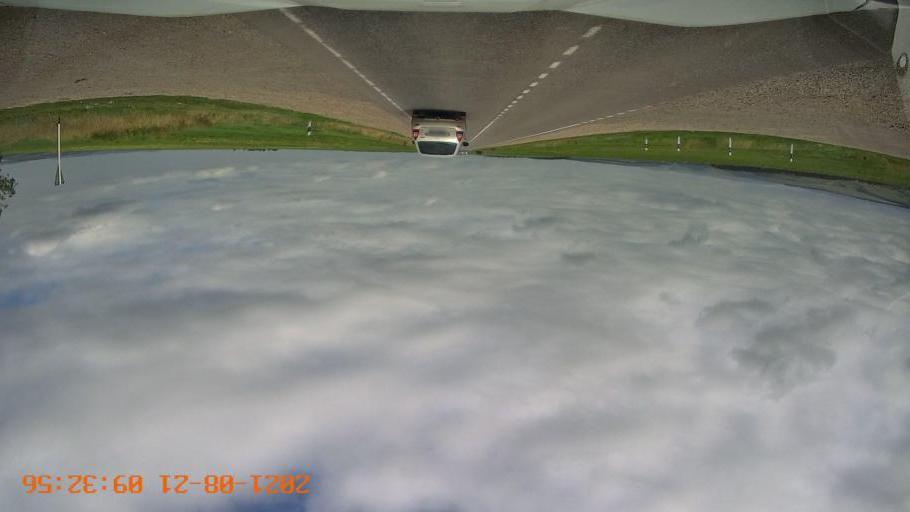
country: RU
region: Stavropol'skiy
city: Yutsa
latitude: 43.9927
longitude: 42.9972
